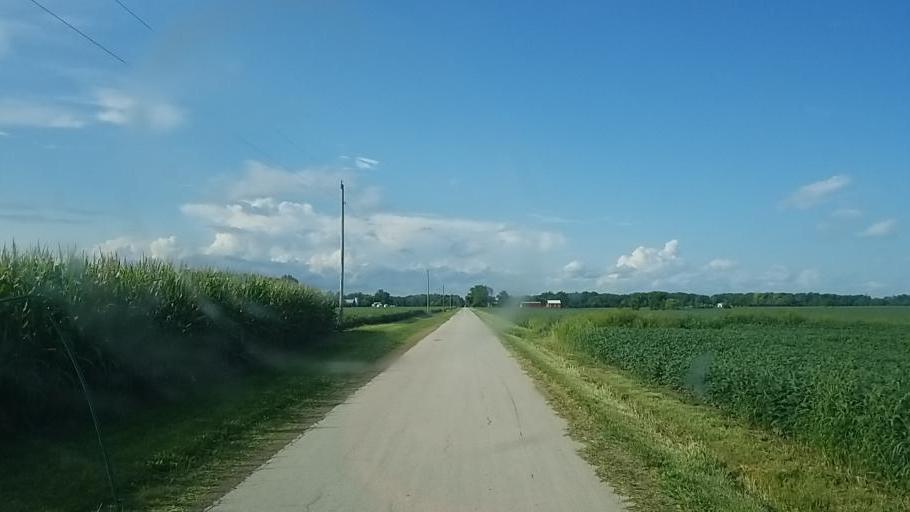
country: US
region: Ohio
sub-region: Wyandot County
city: Upper Sandusky
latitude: 40.7807
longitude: -83.3524
